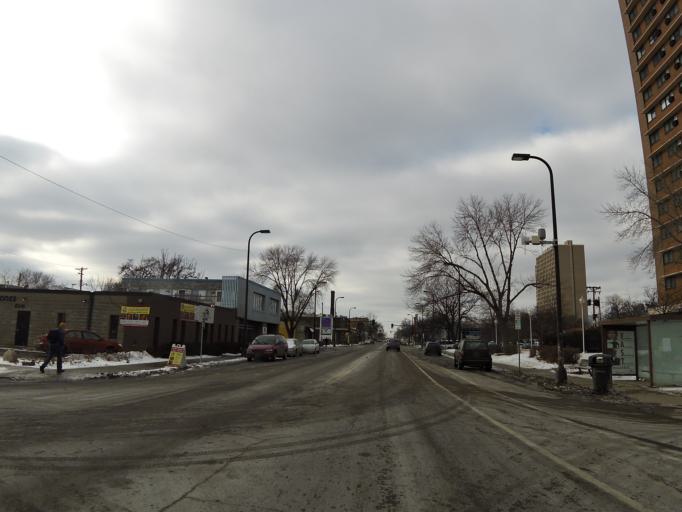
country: US
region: Minnesota
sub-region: Hennepin County
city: Minneapolis
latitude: 44.9628
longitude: -93.2313
